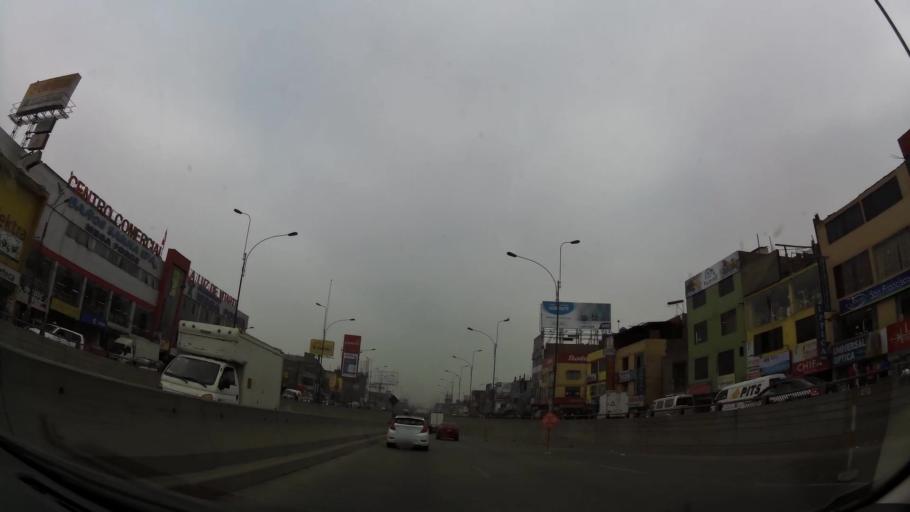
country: PE
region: Lima
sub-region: Lima
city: Vitarte
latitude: -12.0304
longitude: -76.9253
